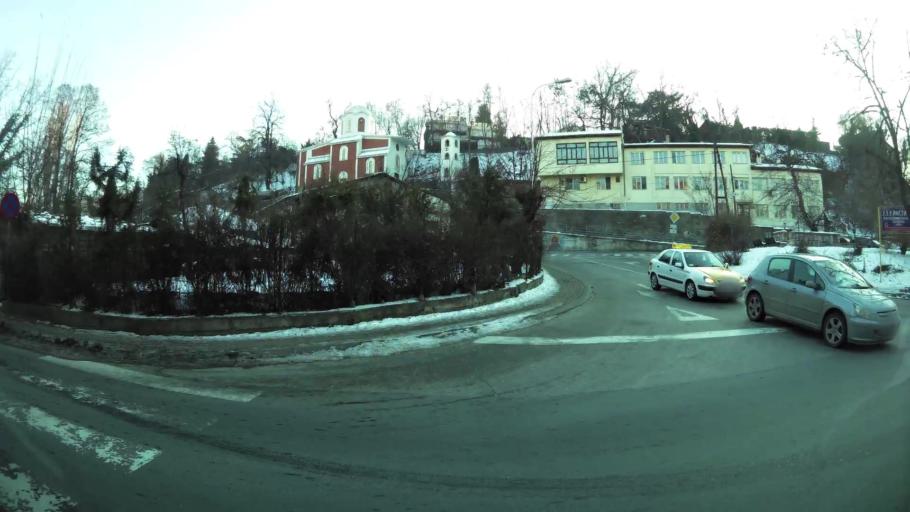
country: MK
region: Karpos
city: Skopje
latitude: 41.9936
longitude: 21.4099
